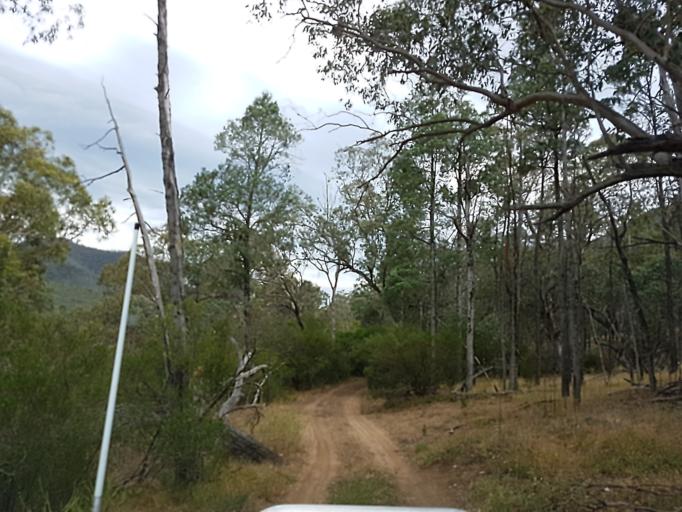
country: AU
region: New South Wales
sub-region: Snowy River
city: Jindabyne
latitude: -36.9592
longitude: 148.4105
